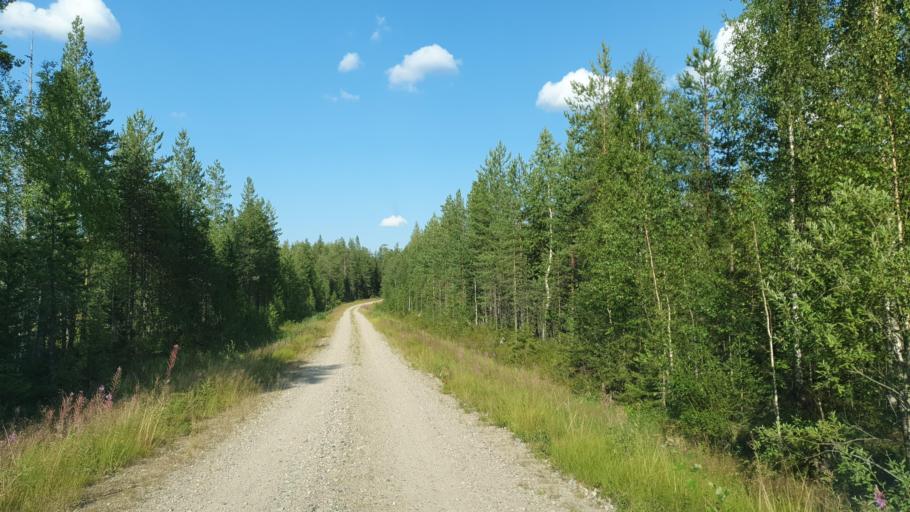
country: FI
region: Kainuu
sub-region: Kehys-Kainuu
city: Kuhmo
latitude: 63.9627
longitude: 29.5382
